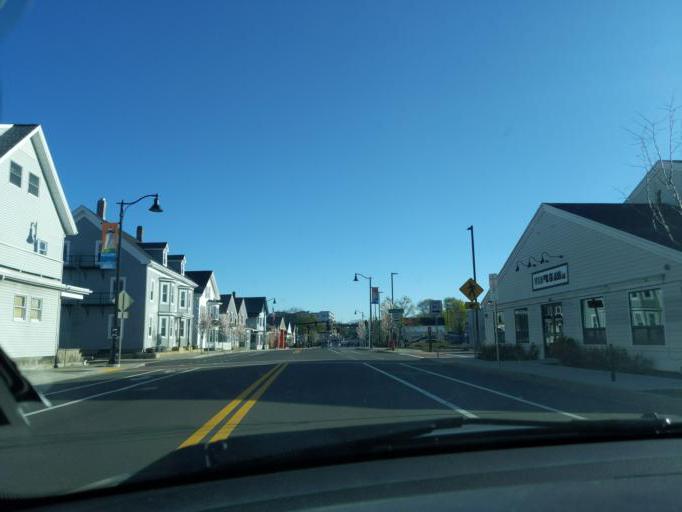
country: US
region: Massachusetts
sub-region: Essex County
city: Beverly
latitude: 42.5533
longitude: -70.8822
